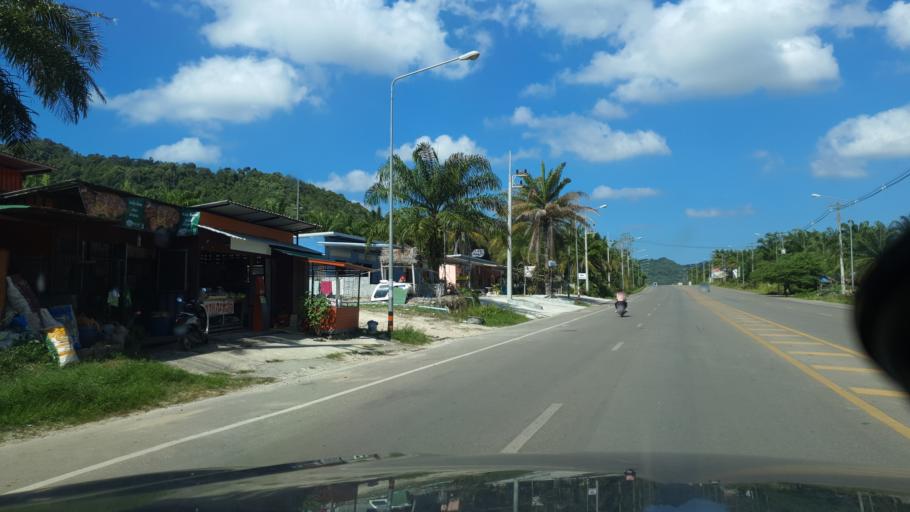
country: TH
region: Phangnga
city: Ban Ao Nang
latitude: 8.0360
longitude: 98.8563
